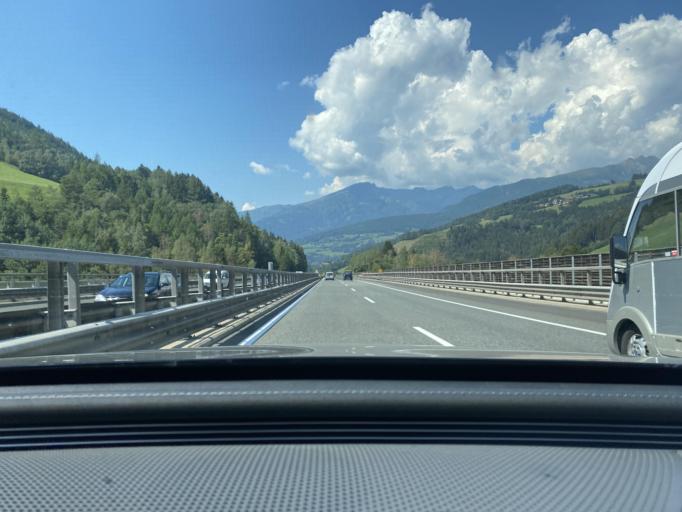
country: AT
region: Carinthia
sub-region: Politischer Bezirk Spittal an der Drau
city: Gmuend
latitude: 46.9205
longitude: 13.5748
